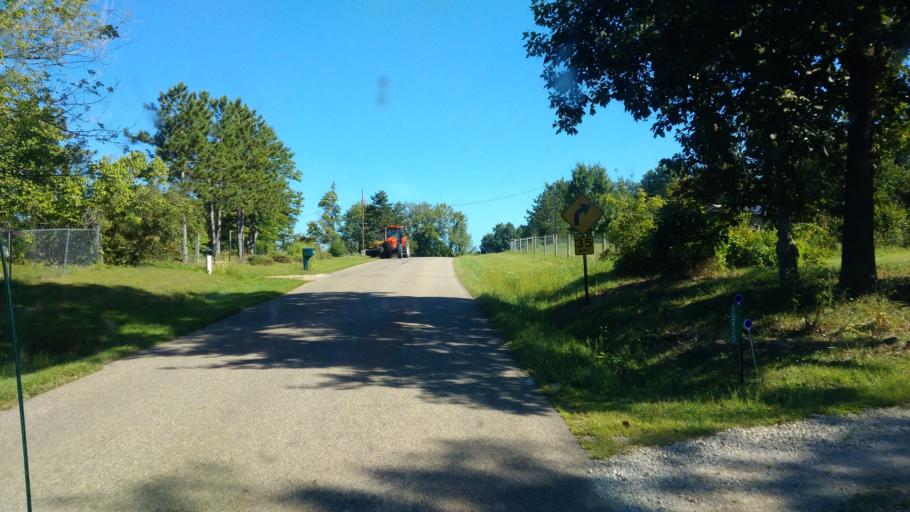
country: US
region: Ohio
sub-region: Knox County
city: Mount Vernon
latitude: 40.4574
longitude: -82.4347
